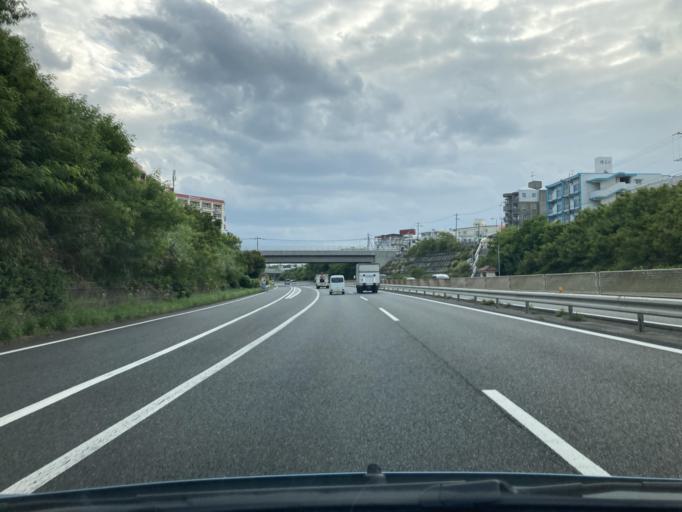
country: JP
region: Okinawa
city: Ginowan
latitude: 26.2562
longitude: 127.7644
